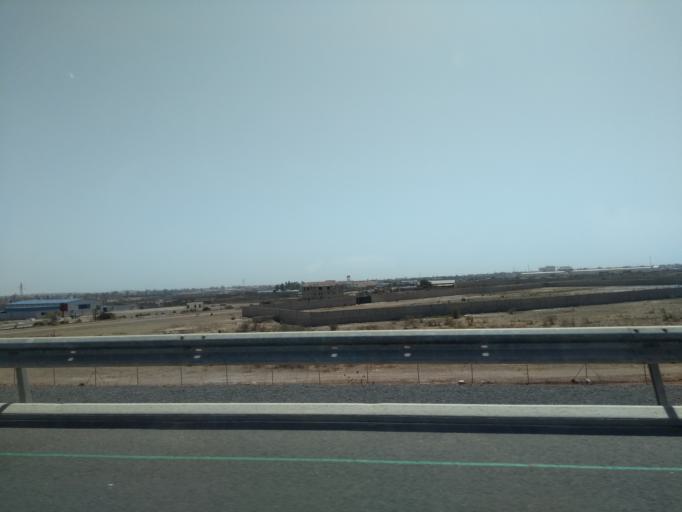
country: SN
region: Thies
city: Pout
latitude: 14.7329
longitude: -17.1607
